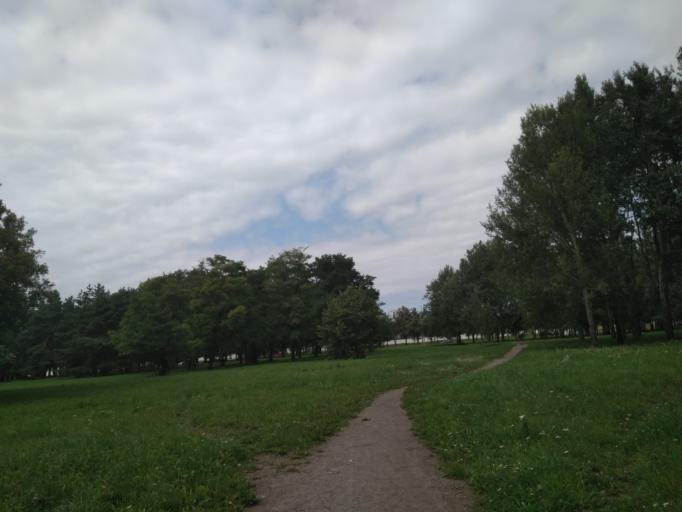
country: BY
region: Minsk
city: Minsk
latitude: 53.9379
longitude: 27.5698
